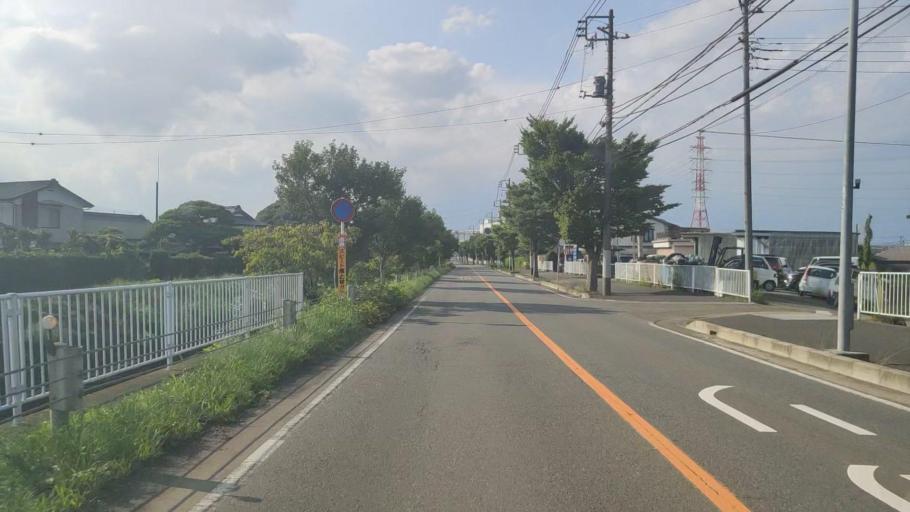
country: JP
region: Kanagawa
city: Isehara
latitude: 35.3988
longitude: 139.3376
